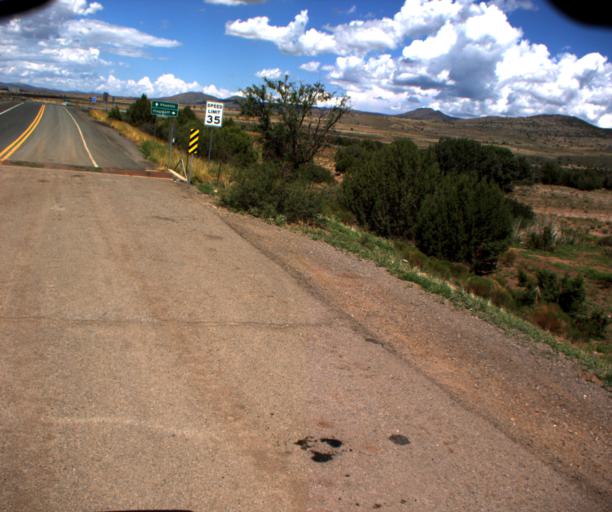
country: US
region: Arizona
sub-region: Yavapai County
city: Camp Verde
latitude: 34.5139
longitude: -111.9897
